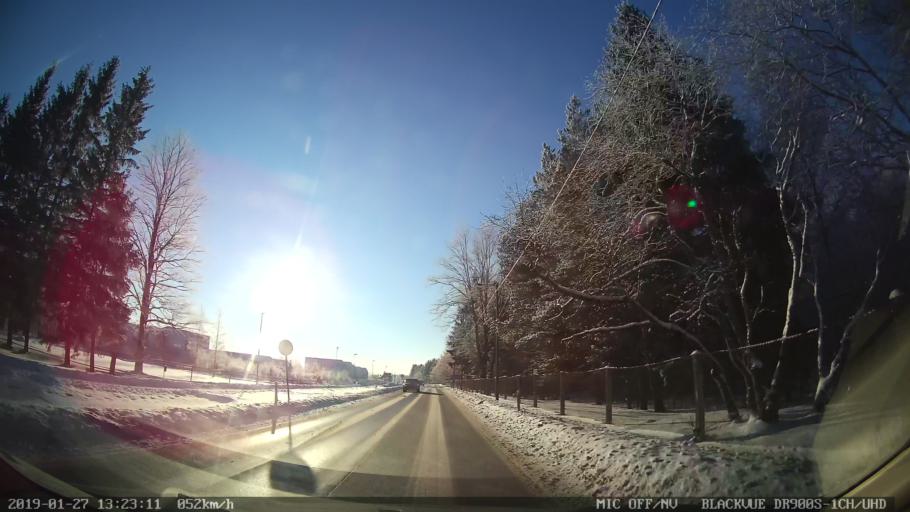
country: EE
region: Harju
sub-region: Tallinna linn
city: Tallinn
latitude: 59.4081
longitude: 24.7965
